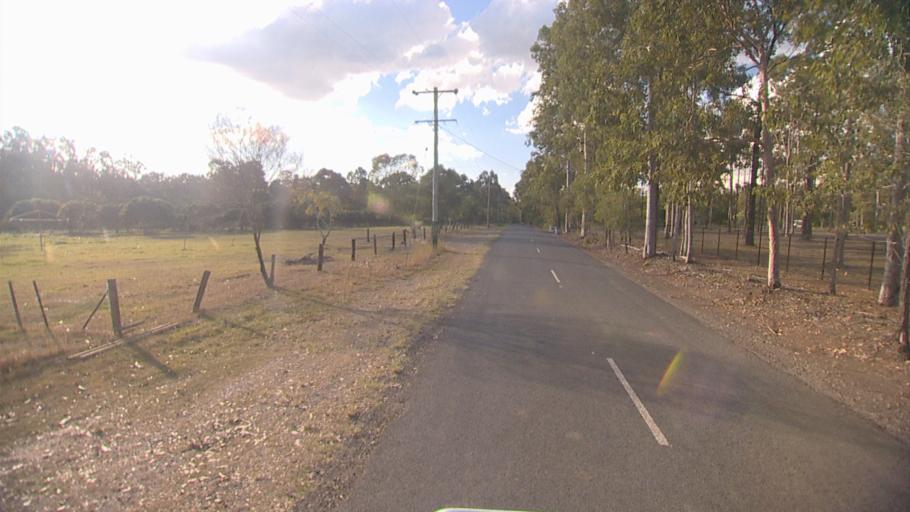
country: AU
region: Queensland
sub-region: Ipswich
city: Springfield Lakes
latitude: -27.6962
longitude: 152.9536
